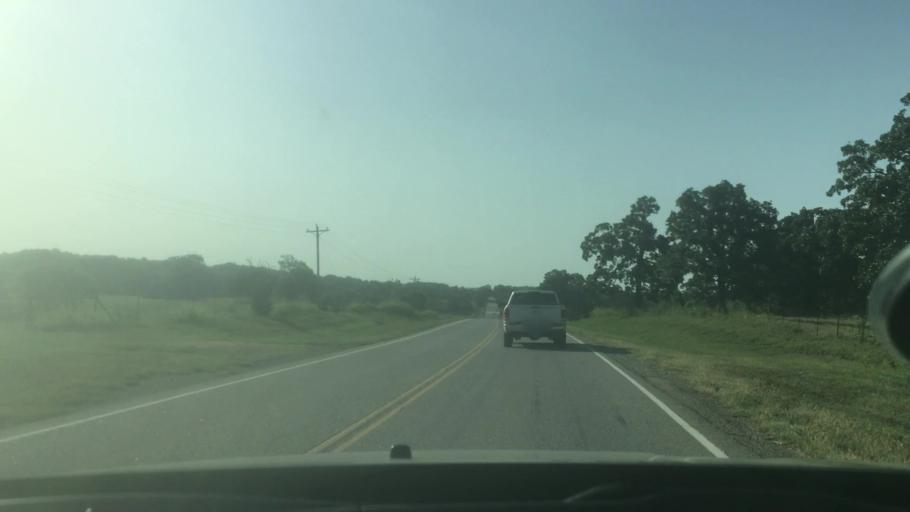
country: US
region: Oklahoma
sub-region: Bryan County
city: Durant
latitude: 34.1737
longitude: -96.4133
